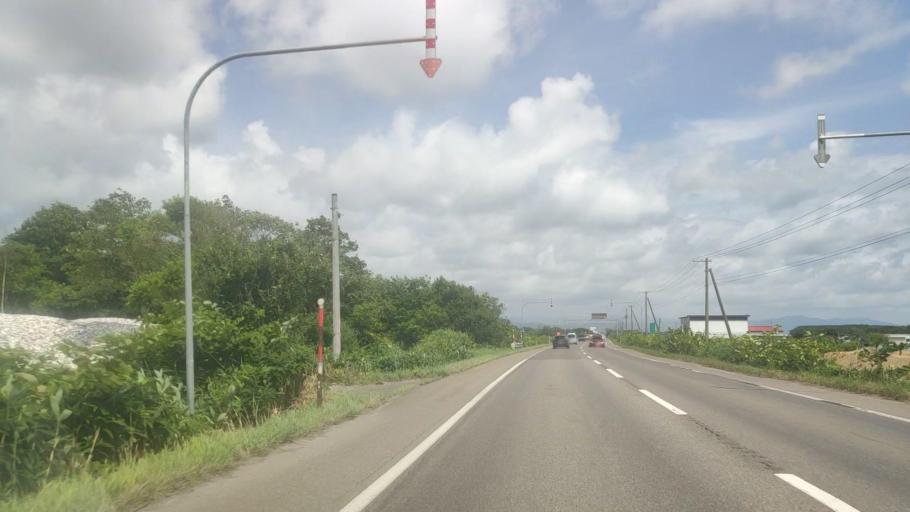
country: JP
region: Hokkaido
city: Niseko Town
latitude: 42.4834
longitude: 140.3521
